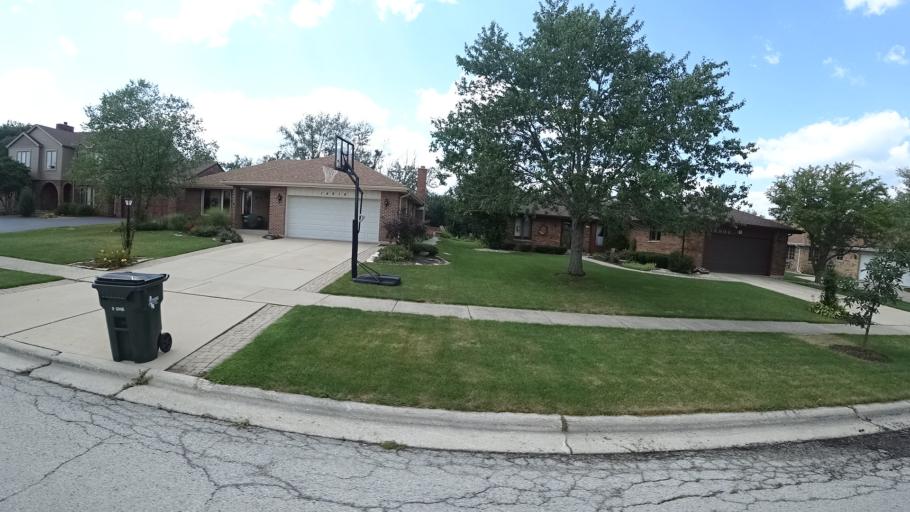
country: US
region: Illinois
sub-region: Cook County
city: Oak Forest
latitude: 41.6208
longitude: -87.7756
